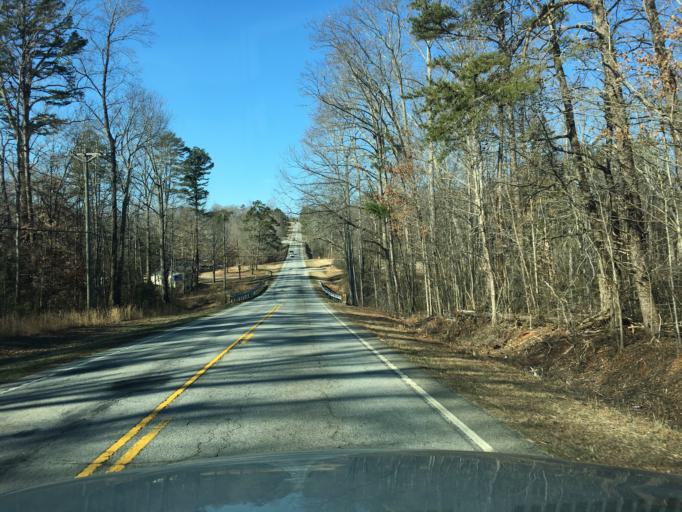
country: US
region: South Carolina
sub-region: Pickens County
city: Easley
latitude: 34.8916
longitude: -82.5508
